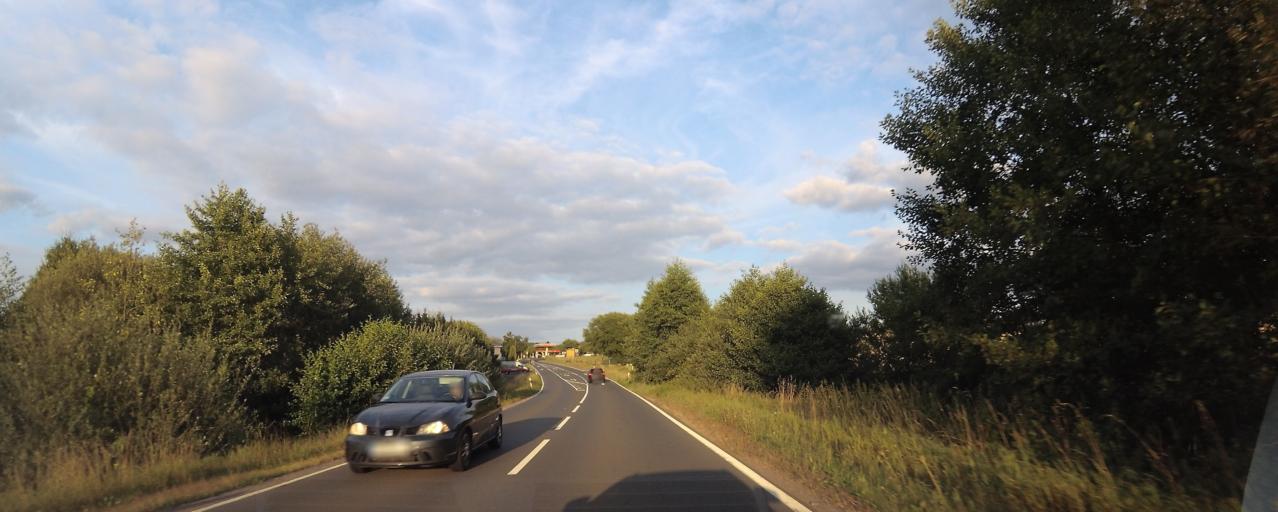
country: DE
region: Rheinland-Pfalz
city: Herforst
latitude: 49.9461
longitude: 6.6871
